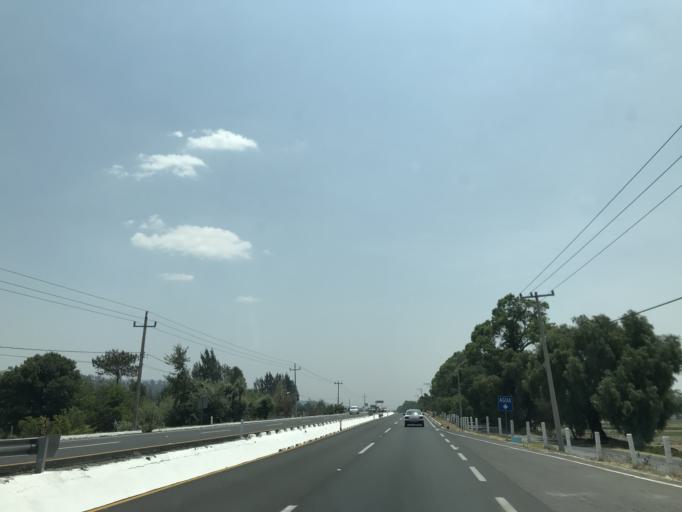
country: MX
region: Tlaxcala
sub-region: Ixtacuixtla de Mariano Matamoros
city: Santa Justina Ecatepec
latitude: 19.3284
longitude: -98.3480
